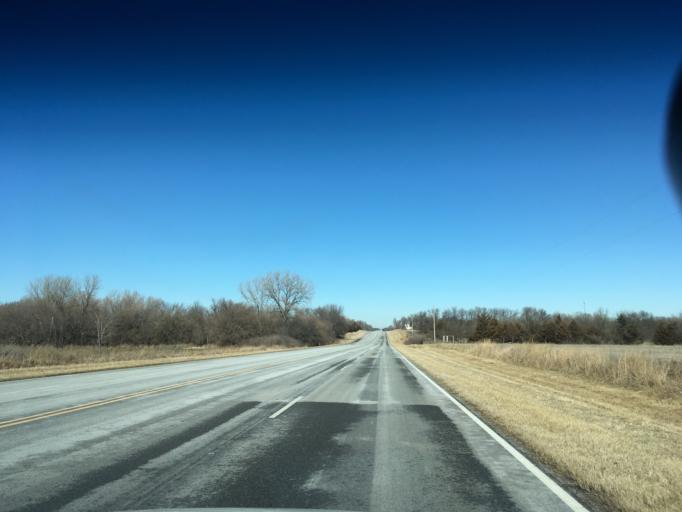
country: US
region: Kansas
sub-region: Harvey County
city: Sedgwick
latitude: 37.9312
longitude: -97.3363
